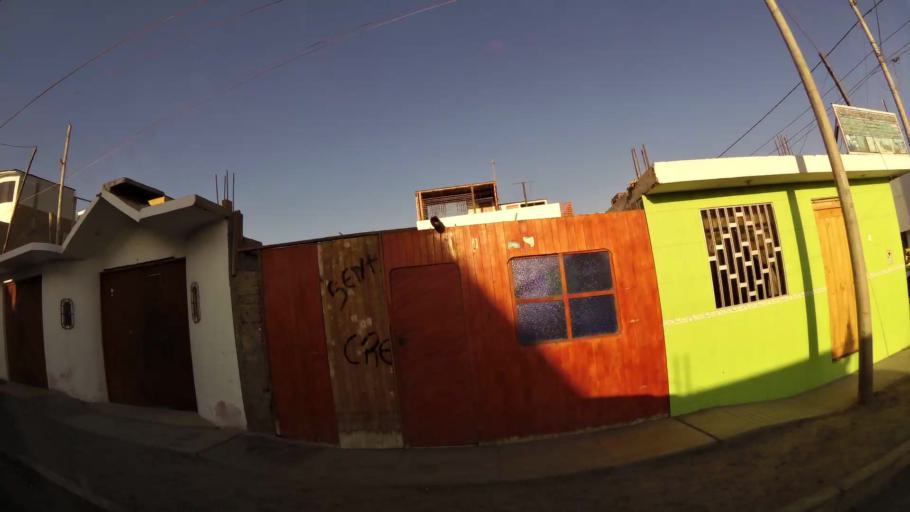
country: PE
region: Ica
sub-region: Provincia de Pisco
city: Villa Tupac Amaru
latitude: -13.7158
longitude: -76.1531
